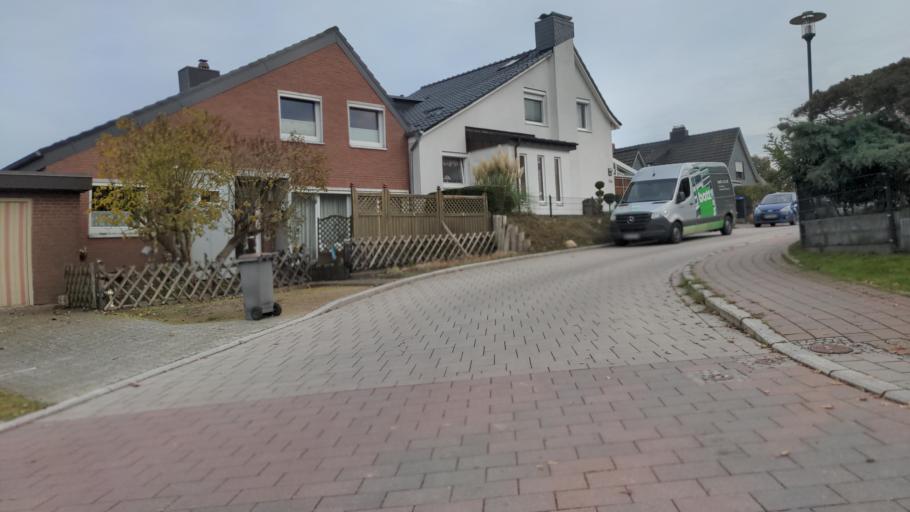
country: DE
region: Schleswig-Holstein
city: Stockelsdorf
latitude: 53.9044
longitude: 10.6572
